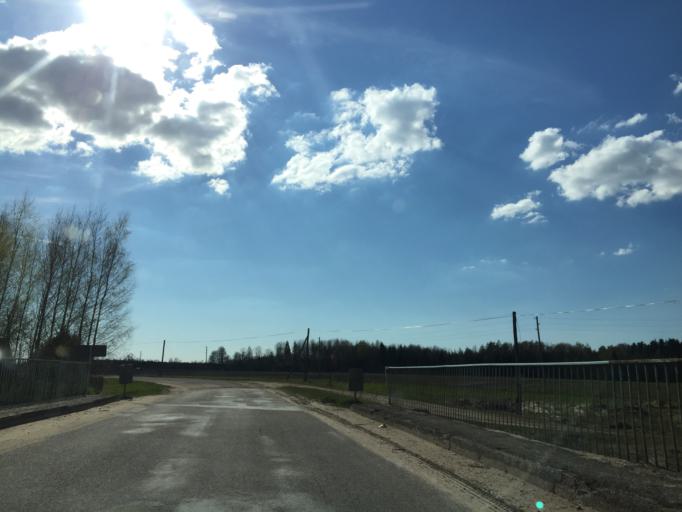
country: LV
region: Saulkrastu
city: Saulkrasti
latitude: 57.3495
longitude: 24.5448
